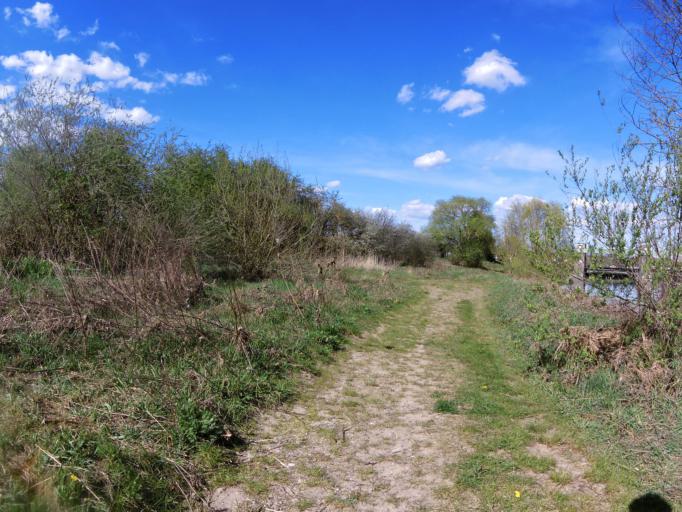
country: DE
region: Bavaria
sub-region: Regierungsbezirk Unterfranken
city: Volkach
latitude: 49.8588
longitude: 10.2168
